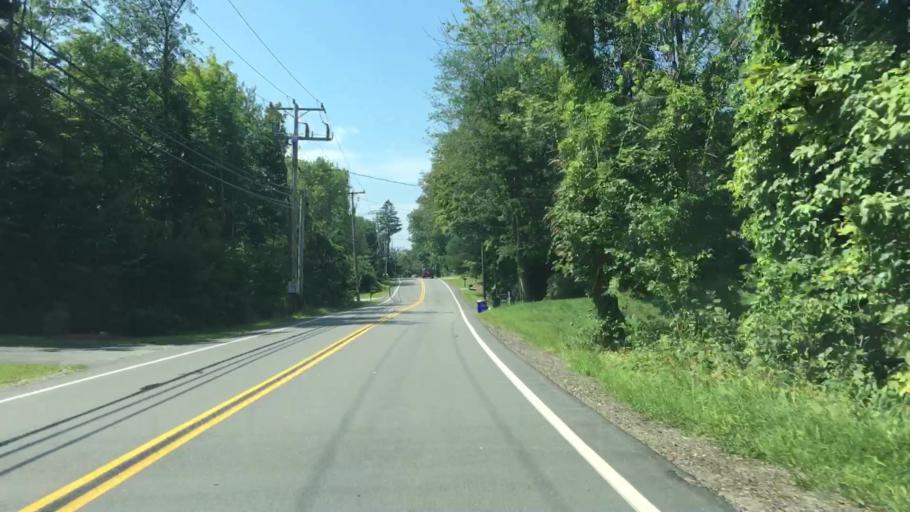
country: US
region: New Hampshire
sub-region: Rockingham County
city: Hampstead
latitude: 42.8769
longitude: -71.1724
